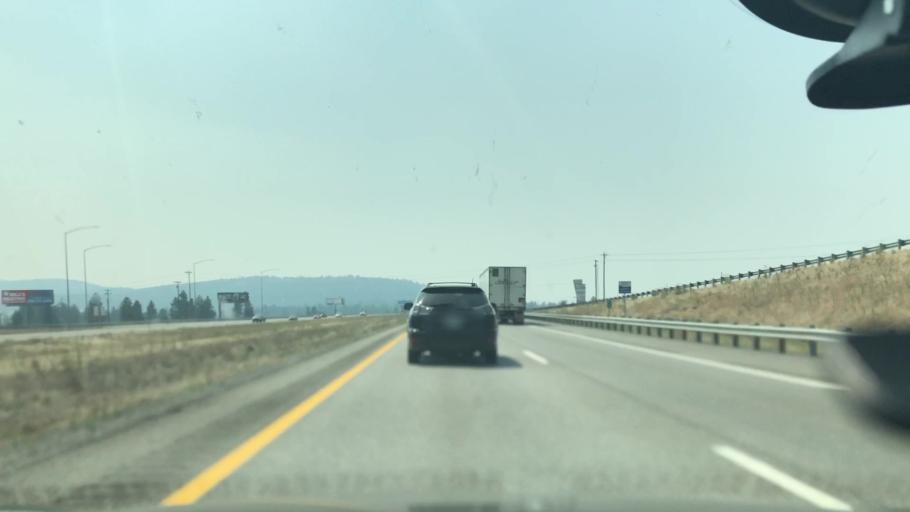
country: US
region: Washington
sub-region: Spokane County
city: Otis Orchards-East Farms
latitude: 47.7014
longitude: -117.0207
